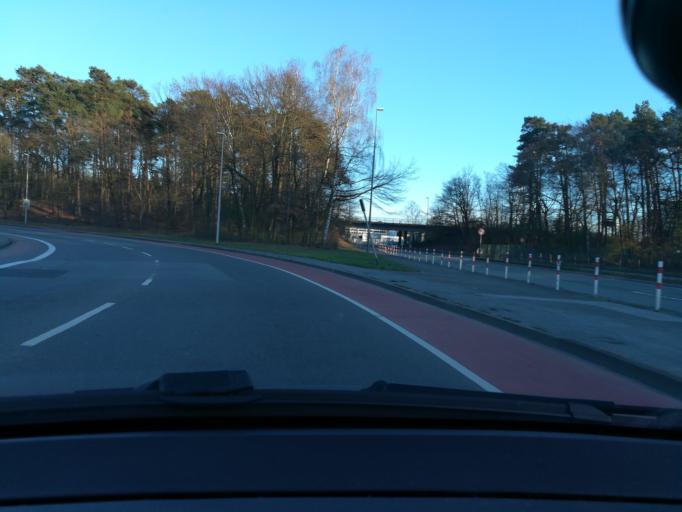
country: DE
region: North Rhine-Westphalia
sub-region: Regierungsbezirk Detmold
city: Oerlinghausen
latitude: 51.9444
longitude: 8.5825
